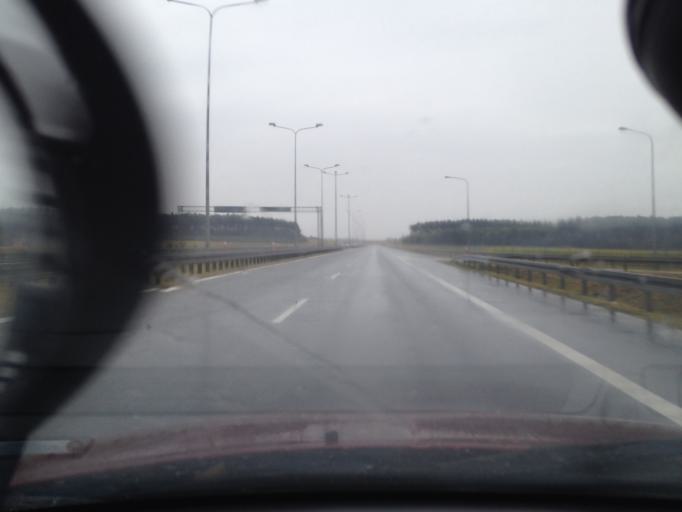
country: PL
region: Lubusz
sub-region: Powiat swiebodzinski
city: Swiebodzin
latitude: 52.3188
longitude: 15.5494
